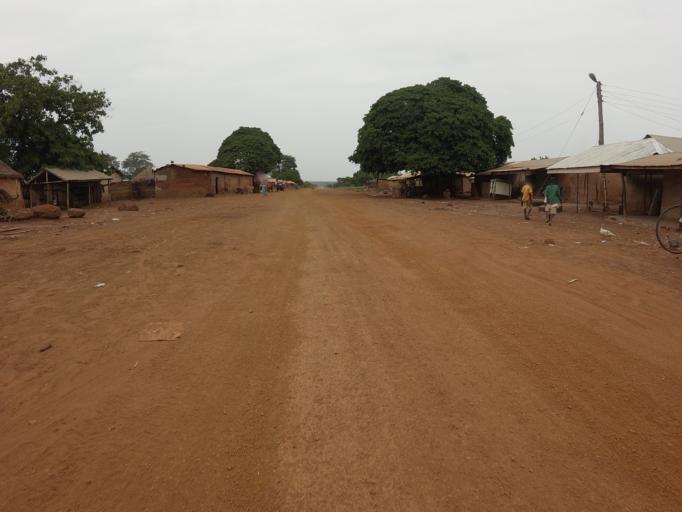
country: GH
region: Northern
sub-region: Yendi
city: Yendi
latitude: 9.2796
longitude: 0.0180
